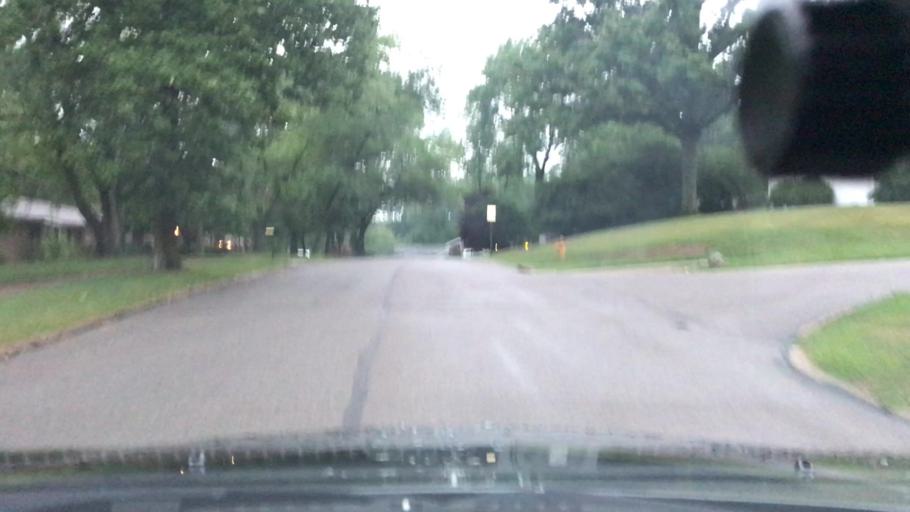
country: US
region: Missouri
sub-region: Saint Louis County
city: Maryland Heights
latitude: 38.6930
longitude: -90.4580
